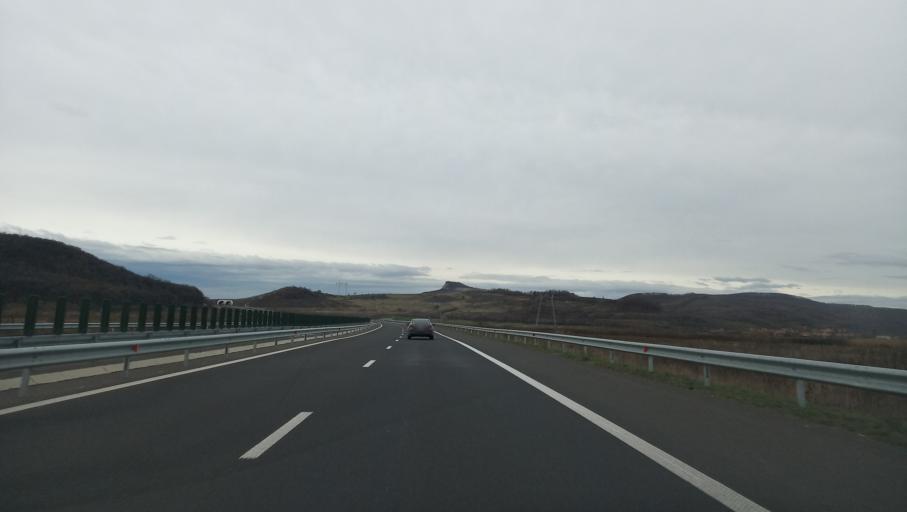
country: RO
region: Hunedoara
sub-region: Comuna Branisca
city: Branisca
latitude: 45.9338
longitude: 22.7585
